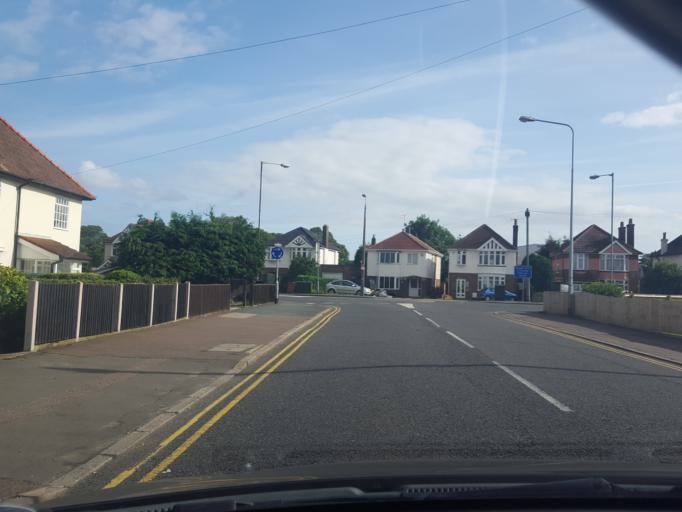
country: GB
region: England
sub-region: Essex
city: Dovercourt
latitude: 51.9350
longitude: 1.2602
